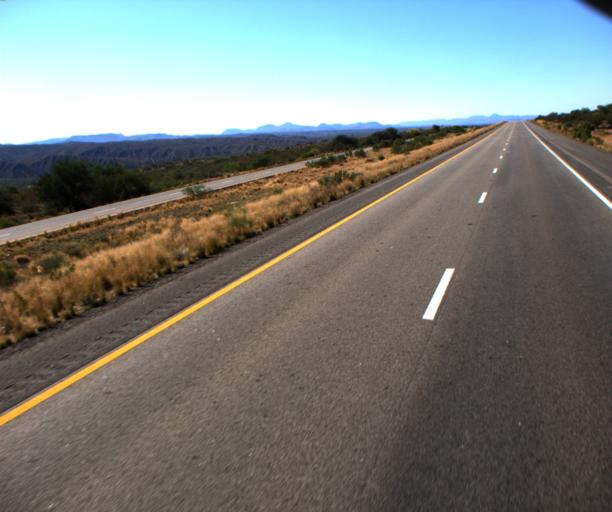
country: US
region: Arizona
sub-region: Mohave County
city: Kingman
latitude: 34.8840
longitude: -113.6495
